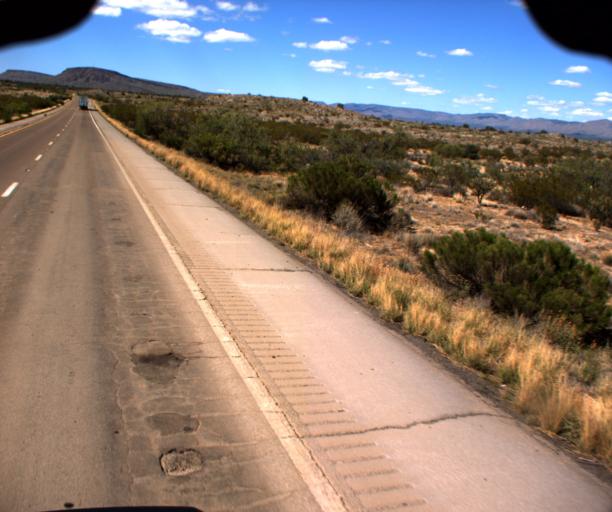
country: US
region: Arizona
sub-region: Mohave County
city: Kingman
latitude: 35.1214
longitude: -113.6662
